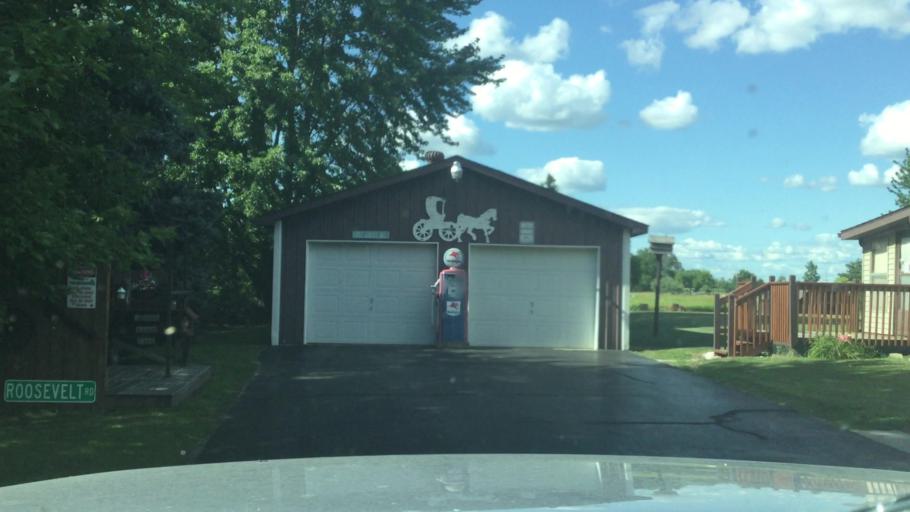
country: US
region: Michigan
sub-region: Saginaw County
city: Saint Charles
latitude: 43.3657
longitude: -84.1695
